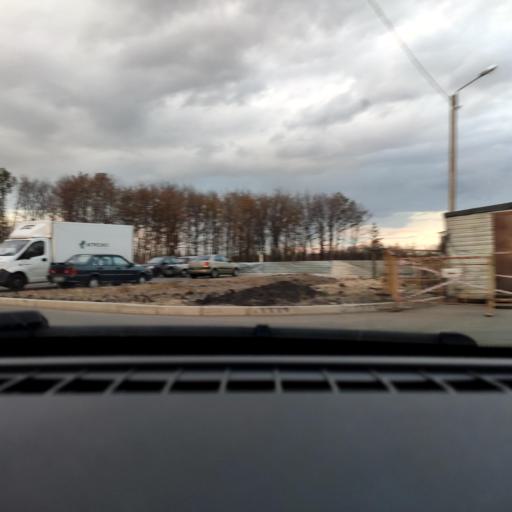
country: RU
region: Voronezj
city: Maslovka
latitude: 51.6334
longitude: 39.2992
